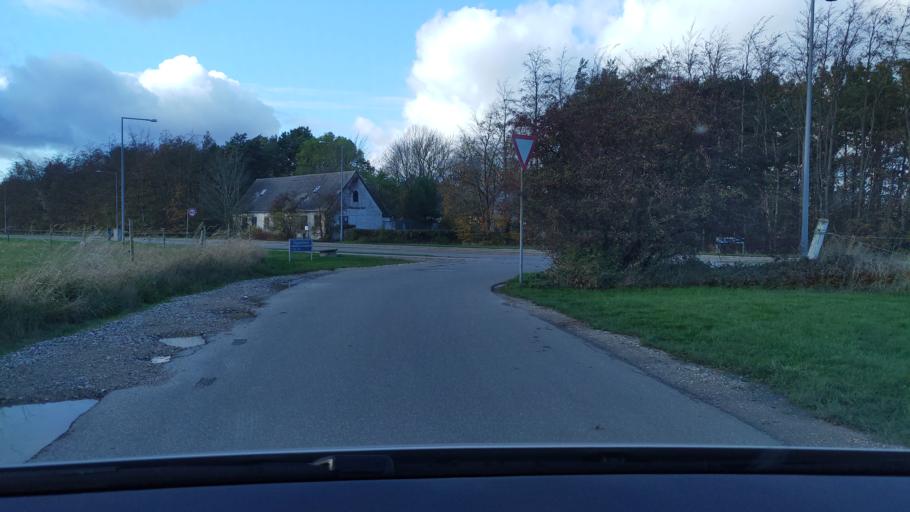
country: DK
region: Capital Region
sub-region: Tarnby Kommune
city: Tarnby
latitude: 55.6069
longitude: 12.6048
